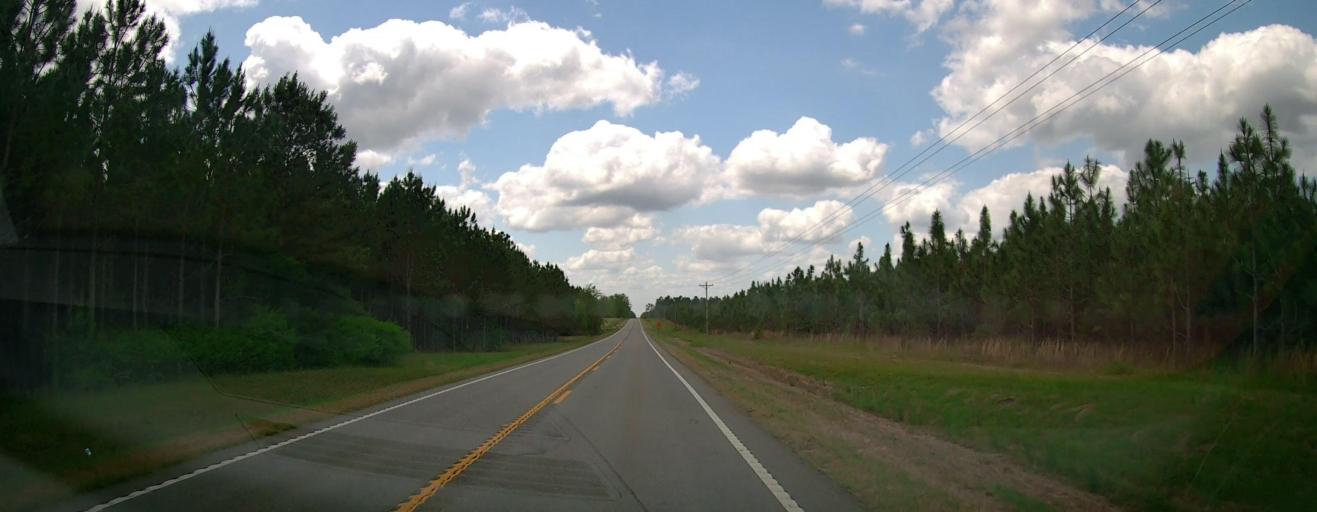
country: US
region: Georgia
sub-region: Laurens County
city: Dublin
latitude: 32.5830
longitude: -83.0159
